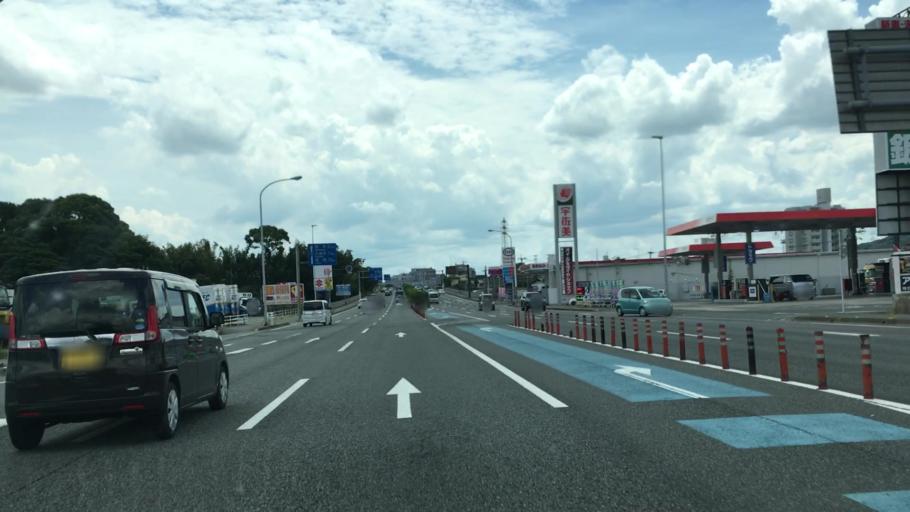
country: JP
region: Fukuoka
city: Chikushino-shi
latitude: 33.4794
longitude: 130.5390
